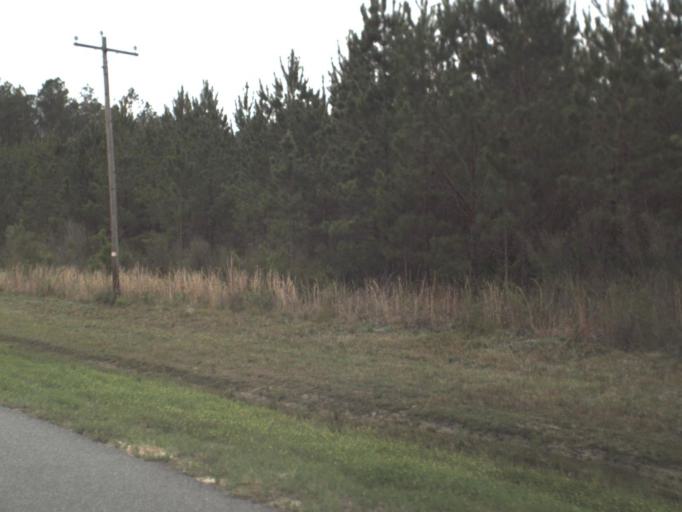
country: US
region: Florida
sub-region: Gulf County
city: Wewahitchka
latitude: 30.3170
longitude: -85.2308
